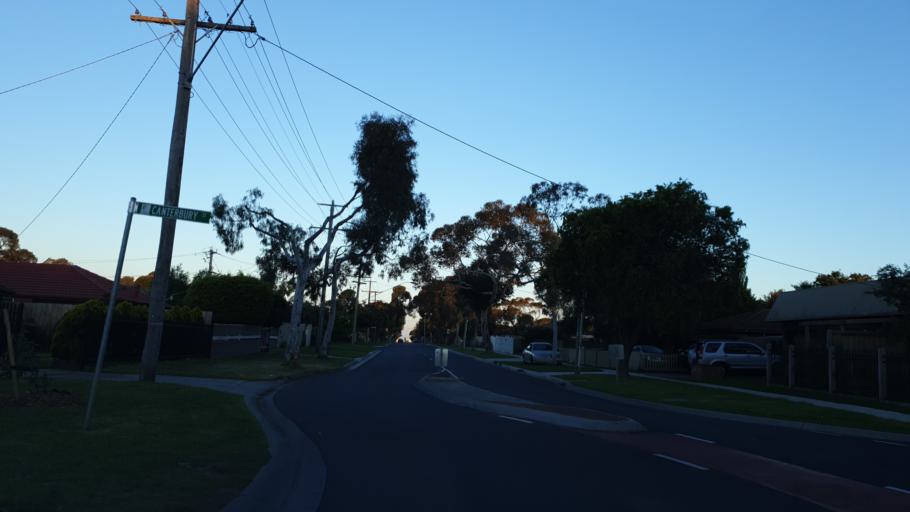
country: AU
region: Victoria
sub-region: Casey
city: Cranbourne
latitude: -38.0983
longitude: 145.2857
